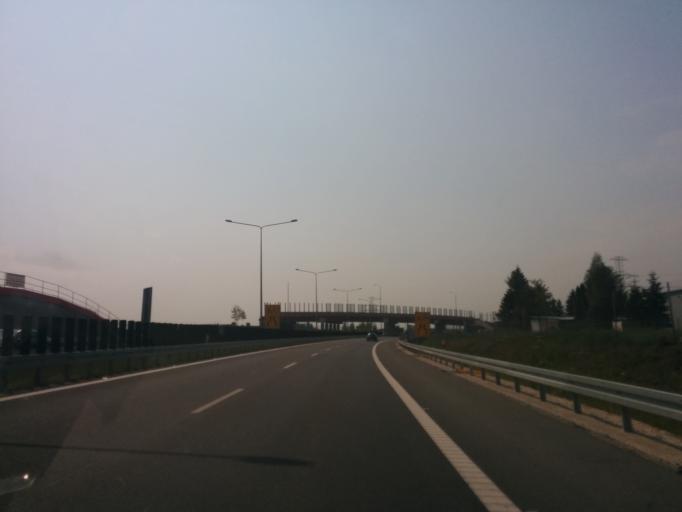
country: PL
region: Masovian Voivodeship
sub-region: Powiat pruszkowski
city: Nowe Grocholice
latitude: 52.1256
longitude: 20.8763
